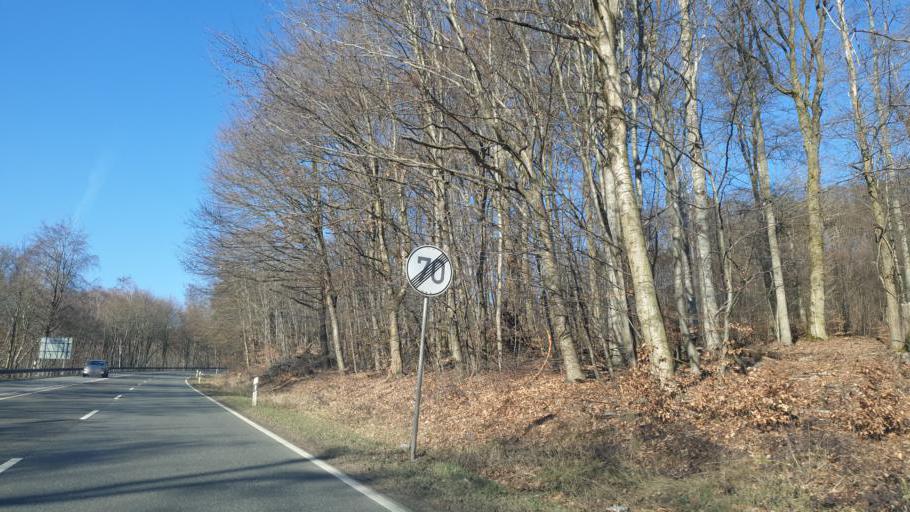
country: DE
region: Hesse
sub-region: Regierungsbezirk Darmstadt
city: Wiesbaden
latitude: 50.1157
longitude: 8.2080
